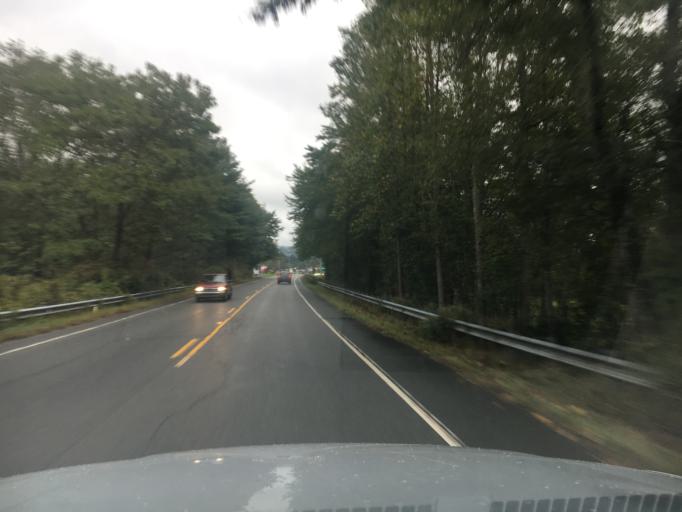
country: US
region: North Carolina
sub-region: Henderson County
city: Etowah
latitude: 35.3167
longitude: -82.6005
